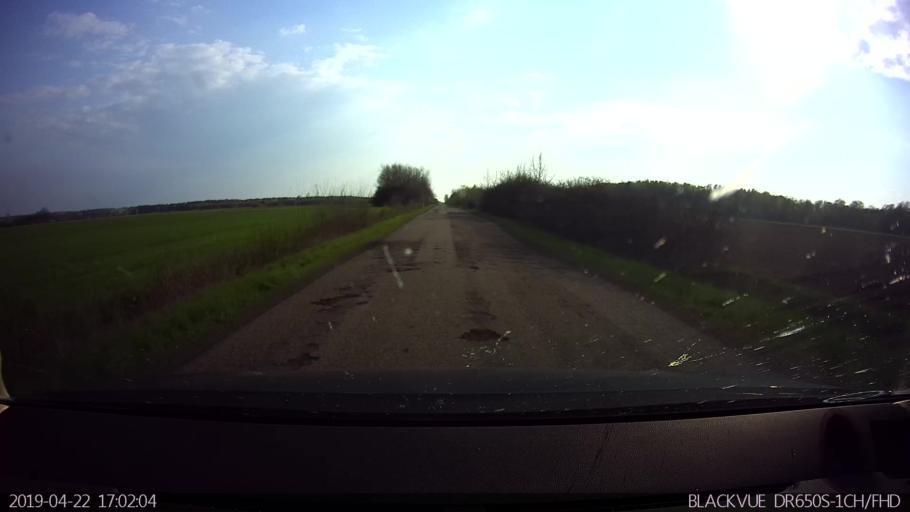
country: PL
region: Podlasie
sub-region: Powiat siemiatycki
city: Drohiczyn
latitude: 52.4310
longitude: 22.7097
